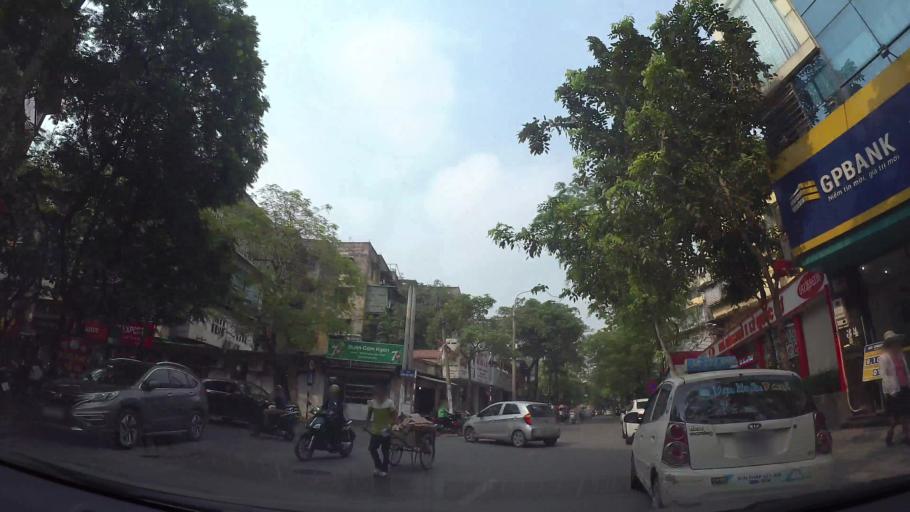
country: VN
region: Ha Noi
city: Cau Giay
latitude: 21.0166
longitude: 105.8109
